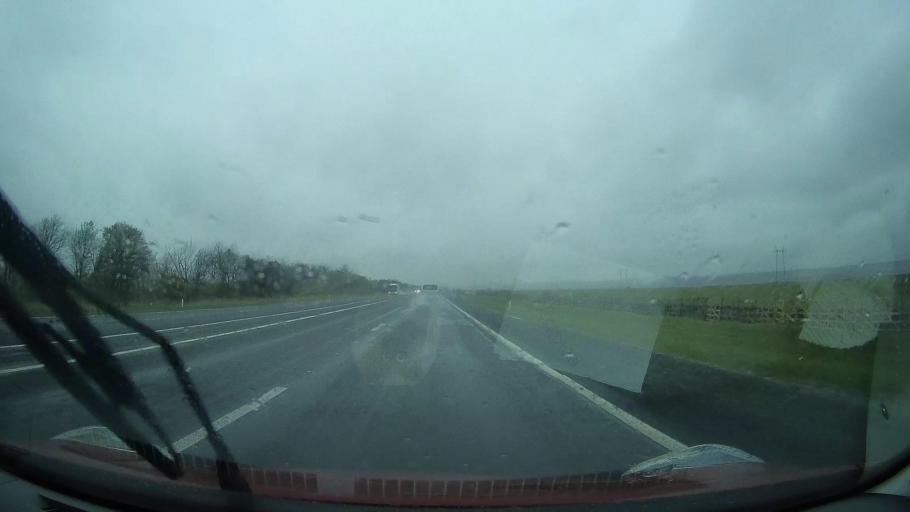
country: RU
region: Stavropol'skiy
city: Nevinnomyssk
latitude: 44.6116
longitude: 42.1205
